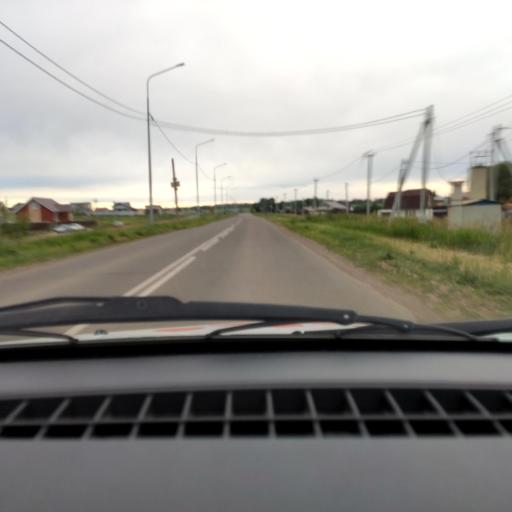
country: RU
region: Bashkortostan
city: Avdon
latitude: 54.5521
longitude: 55.7572
